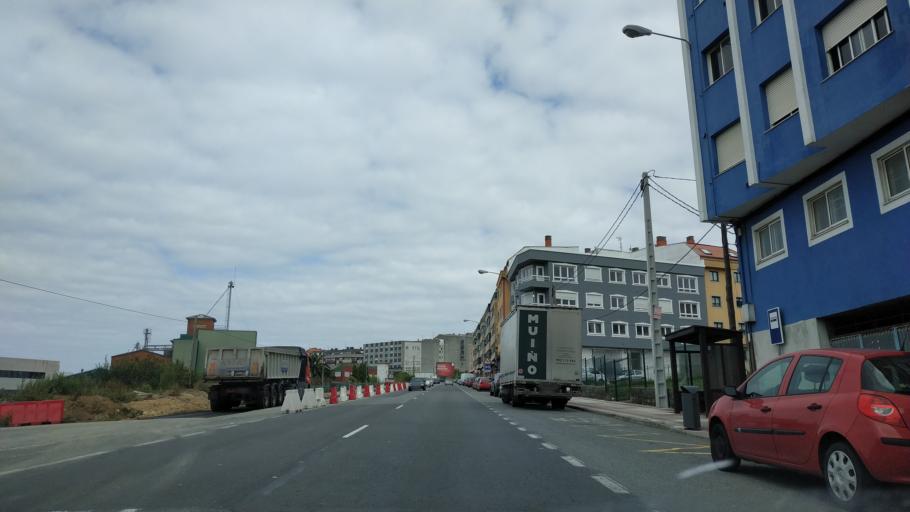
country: ES
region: Galicia
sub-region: Provincia da Coruna
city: Arteixo
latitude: 43.3095
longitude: -8.5031
